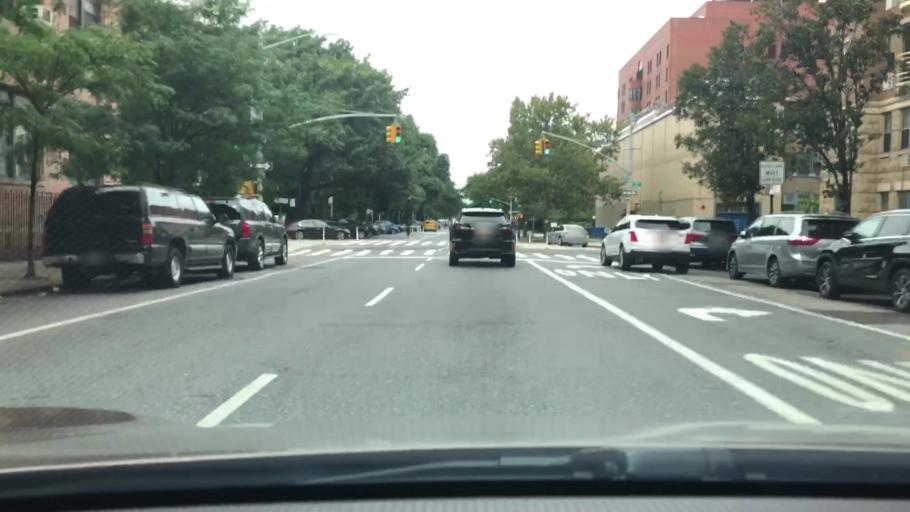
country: US
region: New York
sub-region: New York County
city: Manhattan
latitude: 40.8023
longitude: -73.9432
